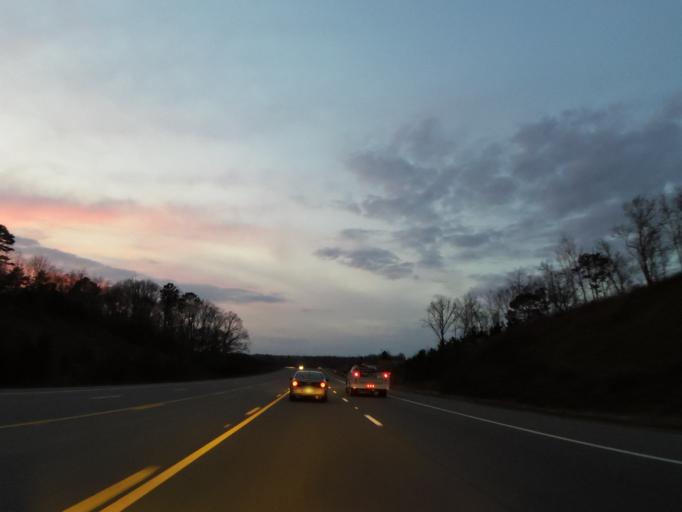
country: US
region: Tennessee
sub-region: Polk County
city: Benton
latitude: 35.1676
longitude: -84.6677
